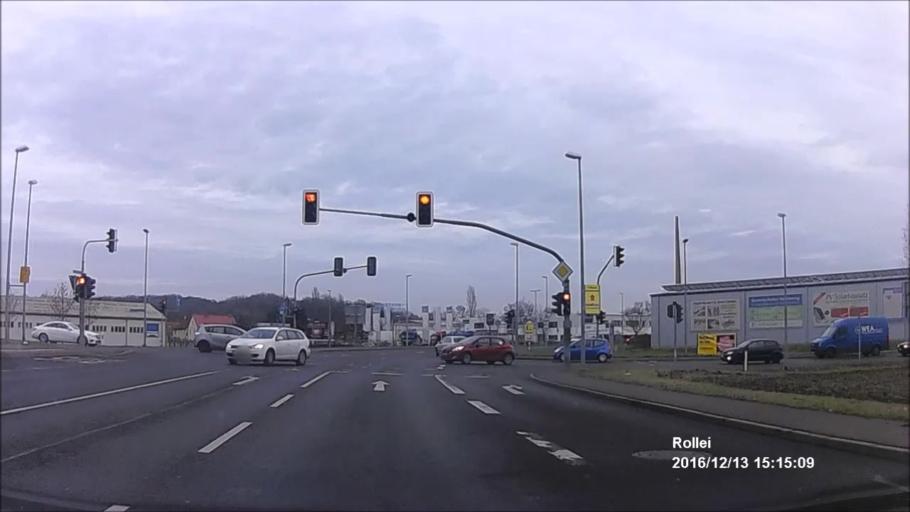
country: DE
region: Thuringia
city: Noda
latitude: 51.0255
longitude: 11.0076
